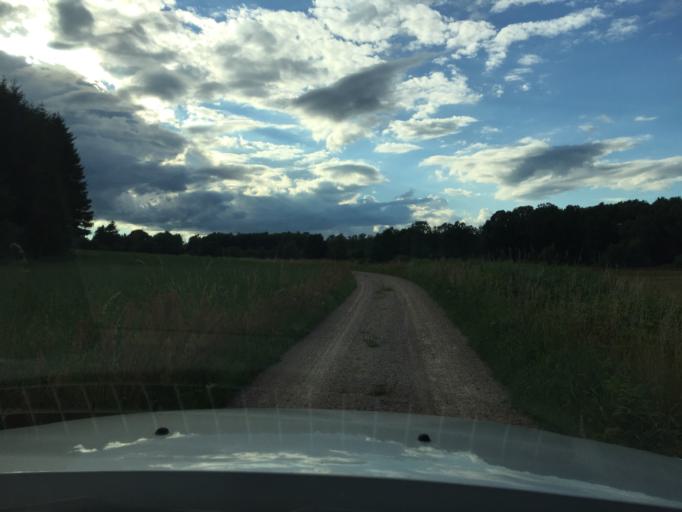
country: SE
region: Skane
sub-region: Hassleholms Kommun
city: Sosdala
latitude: 56.0472
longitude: 13.7097
